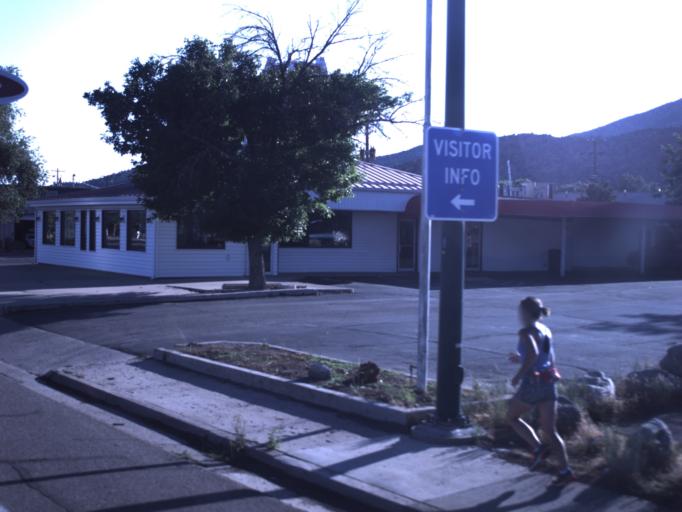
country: US
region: Utah
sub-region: Iron County
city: Cedar City
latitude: 37.6867
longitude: -113.0618
